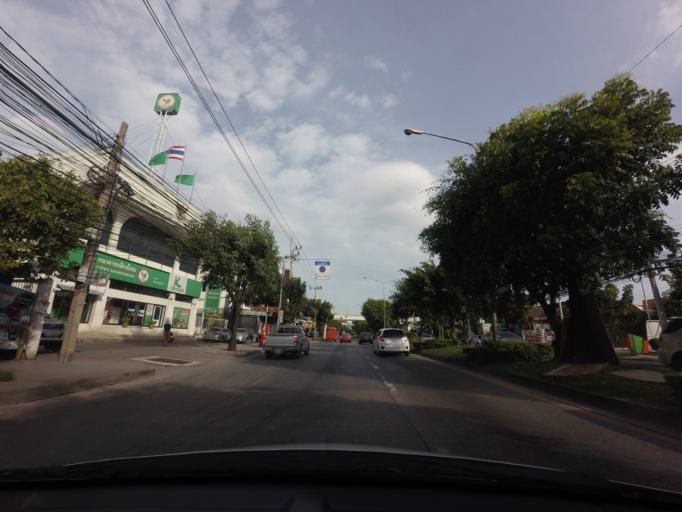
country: TH
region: Bangkok
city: Bueng Kum
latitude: 13.7935
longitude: 100.6521
